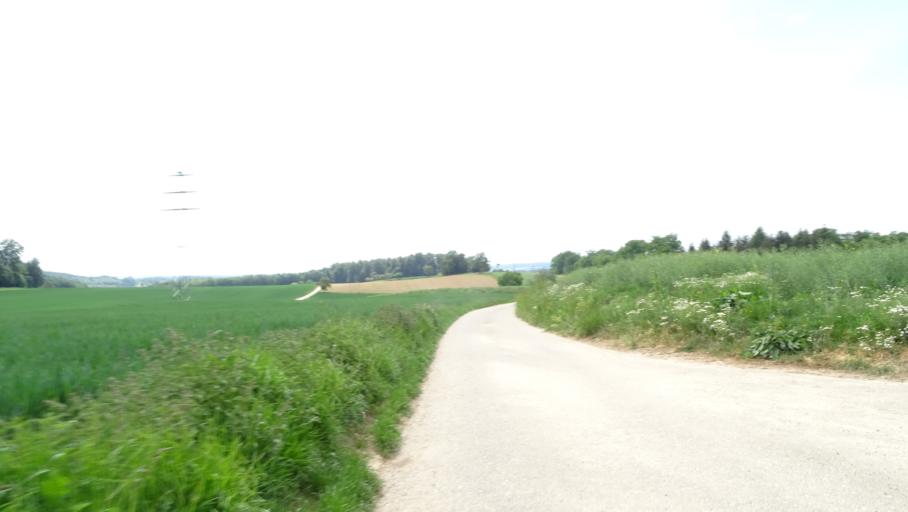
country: DE
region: Baden-Wuerttemberg
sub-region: Karlsruhe Region
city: Binau
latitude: 49.3777
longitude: 9.0489
